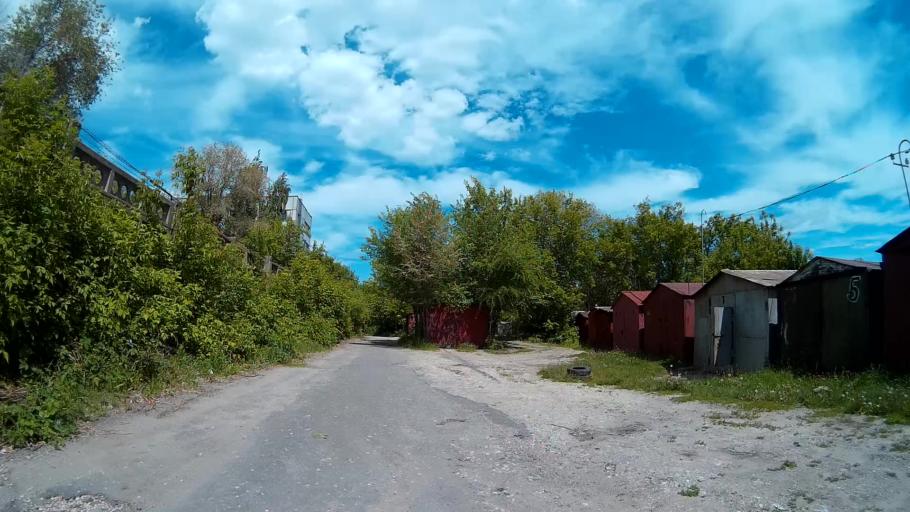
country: RU
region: Ulyanovsk
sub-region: Ulyanovskiy Rayon
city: Ulyanovsk
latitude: 54.2847
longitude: 48.3662
